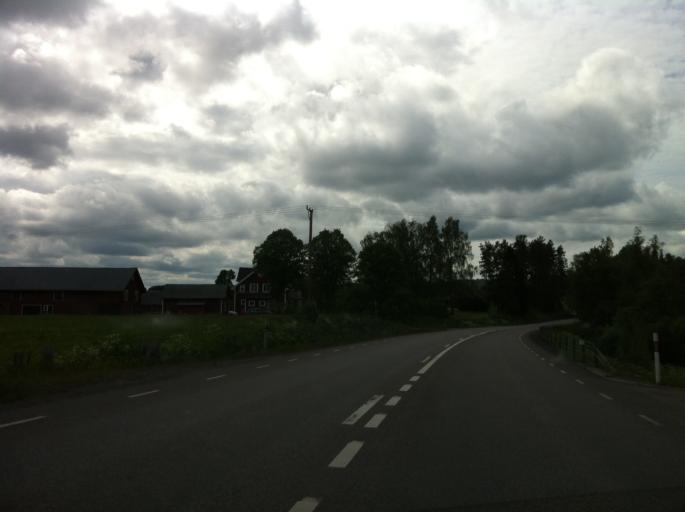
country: SE
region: Vaermland
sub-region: Sunne Kommun
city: Sunne
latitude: 59.7933
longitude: 13.1012
